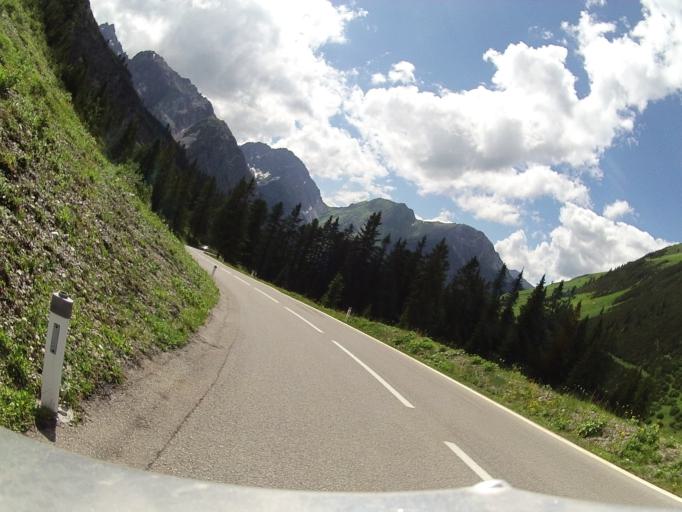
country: AT
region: Tyrol
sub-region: Politischer Bezirk Reutte
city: Namlos
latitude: 47.2845
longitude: 10.6383
